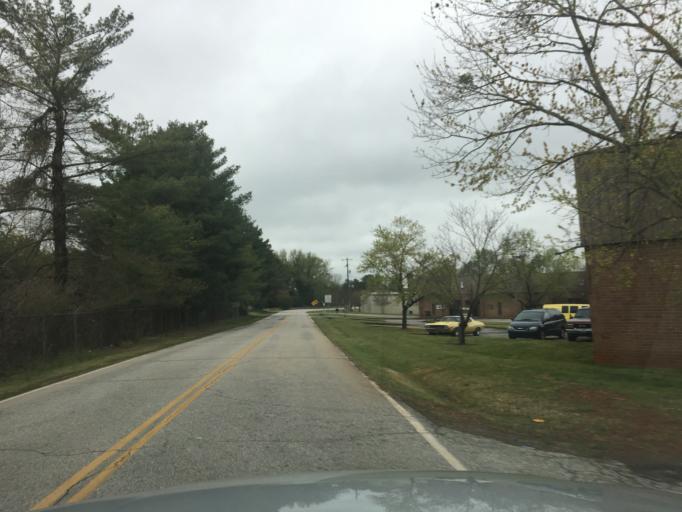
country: US
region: South Carolina
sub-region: Spartanburg County
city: Southern Shops
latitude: 34.9731
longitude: -82.0039
